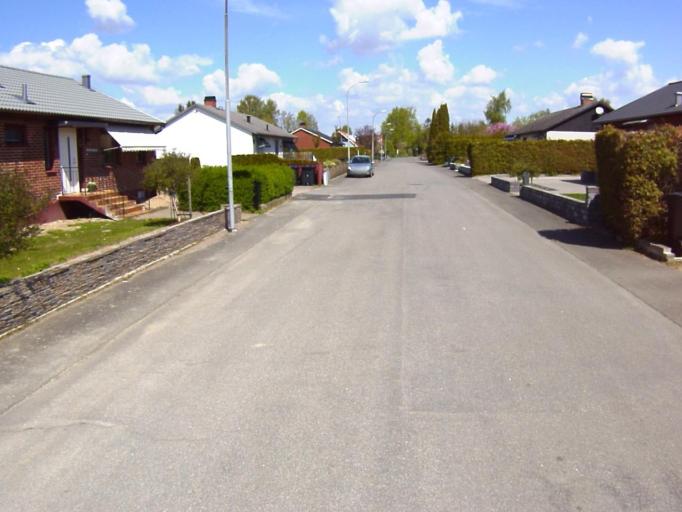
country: SE
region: Skane
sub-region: Kristianstads Kommun
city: Fjalkinge
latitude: 56.0136
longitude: 14.2295
